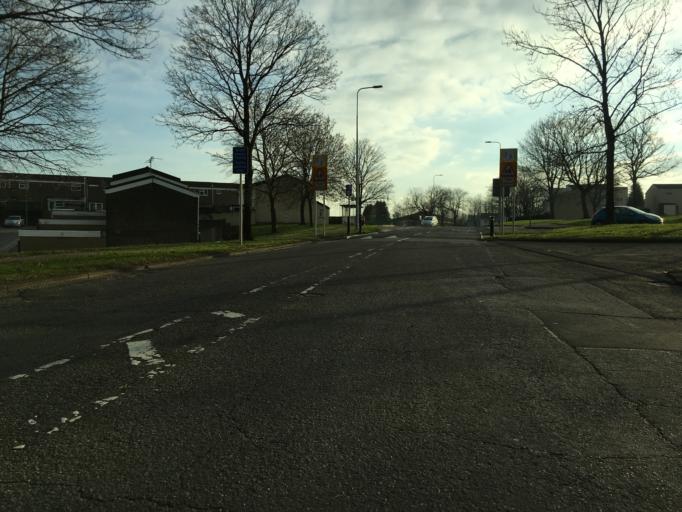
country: GB
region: Wales
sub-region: Cardiff
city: Cardiff
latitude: 51.5181
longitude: -3.1516
